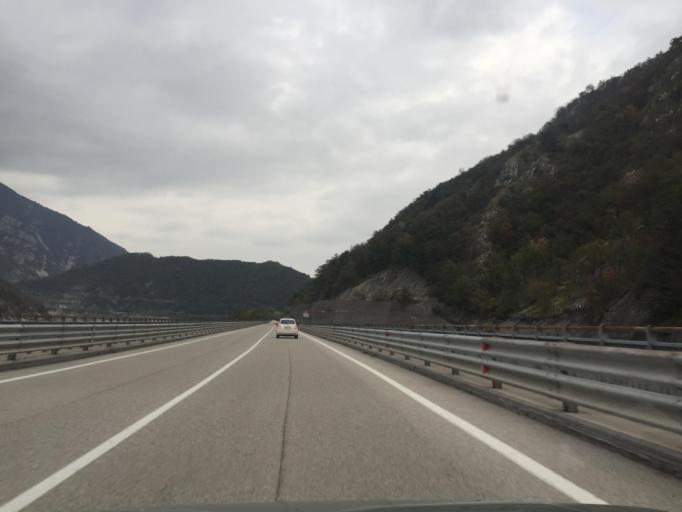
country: IT
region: Friuli Venezia Giulia
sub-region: Provincia di Pordenone
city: Montereale Valcellina
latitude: 46.1649
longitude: 12.6371
